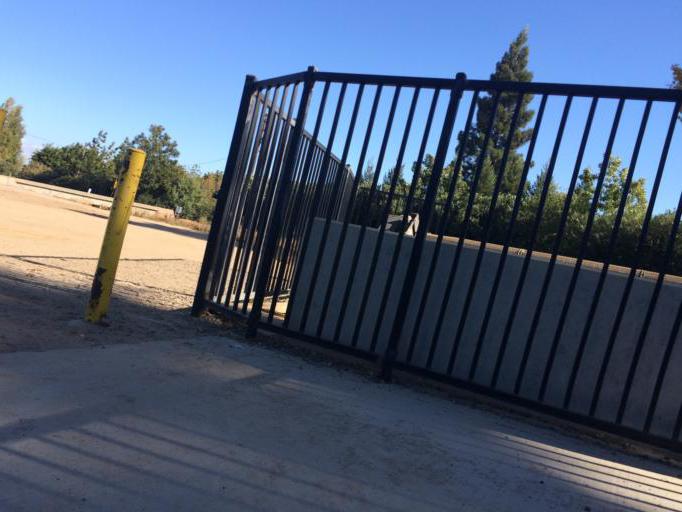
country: US
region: California
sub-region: Fresno County
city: Clovis
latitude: 36.8654
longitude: -119.6938
